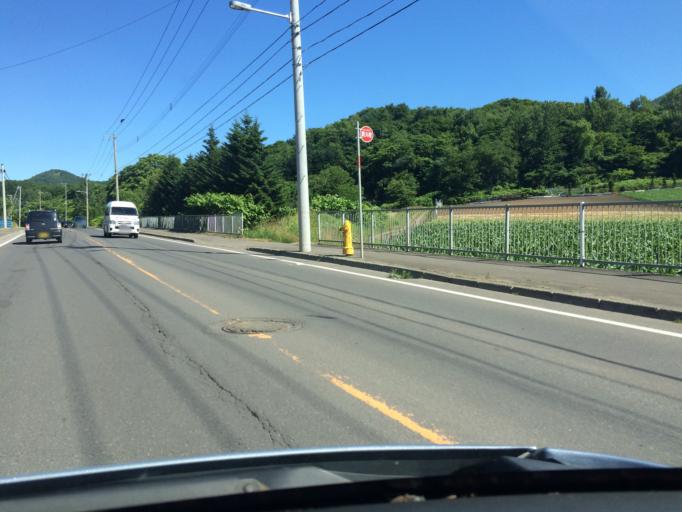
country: JP
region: Hokkaido
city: Sapporo
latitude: 43.0053
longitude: 141.3161
